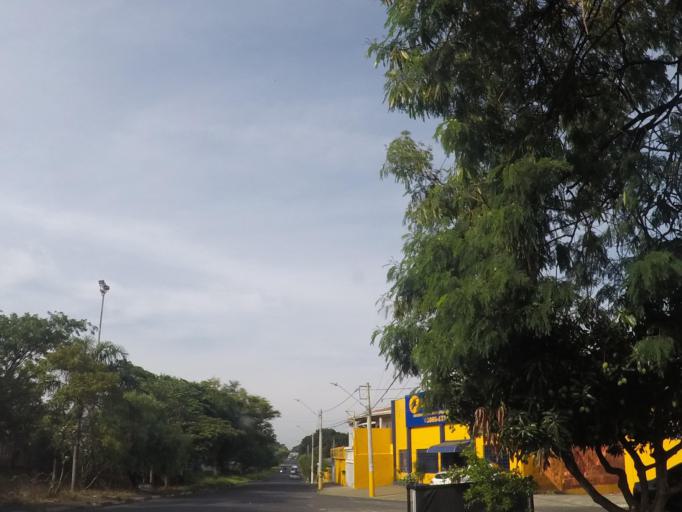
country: BR
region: Sao Paulo
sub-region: Hortolandia
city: Hortolandia
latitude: -22.8563
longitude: -47.1949
